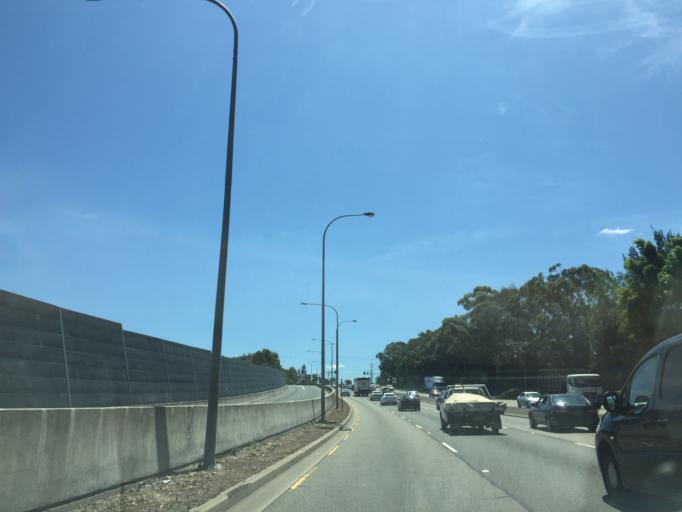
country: AU
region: New South Wales
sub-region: Parramatta
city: Constitution Hill
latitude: -33.7930
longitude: 150.9818
